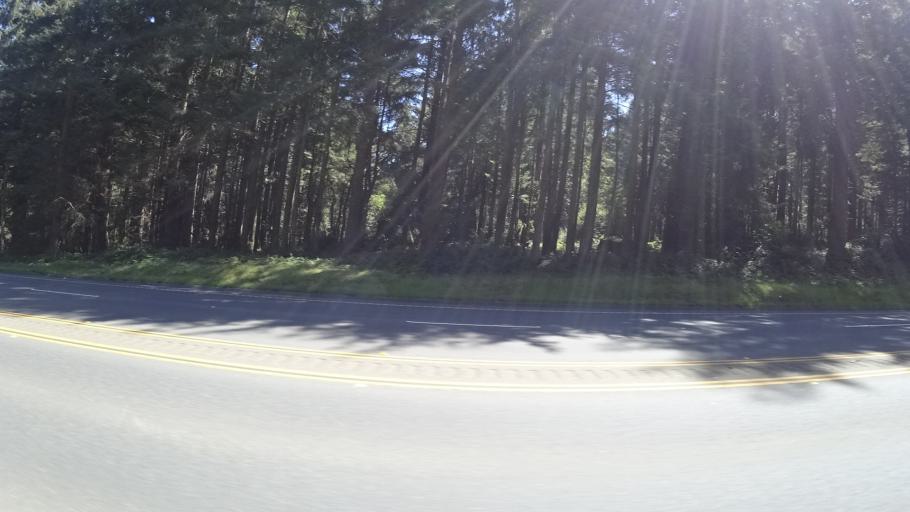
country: US
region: California
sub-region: Humboldt County
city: Westhaven-Moonstone
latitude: 41.1469
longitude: -124.1361
